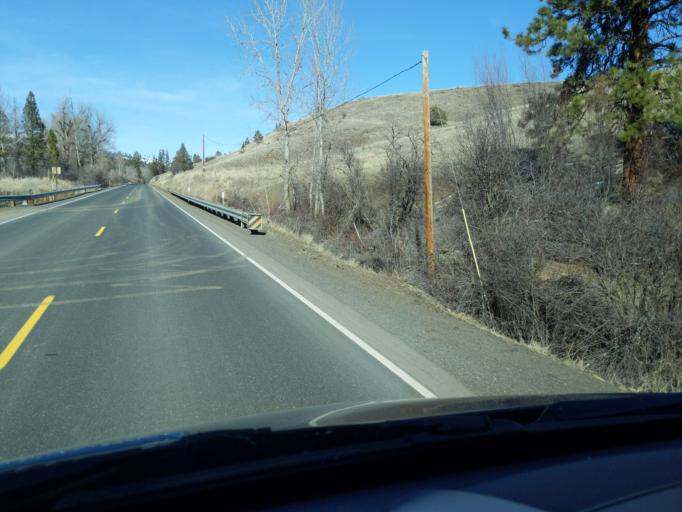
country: US
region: Oregon
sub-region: Grant County
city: John Day
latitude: 44.8483
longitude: -119.0312
